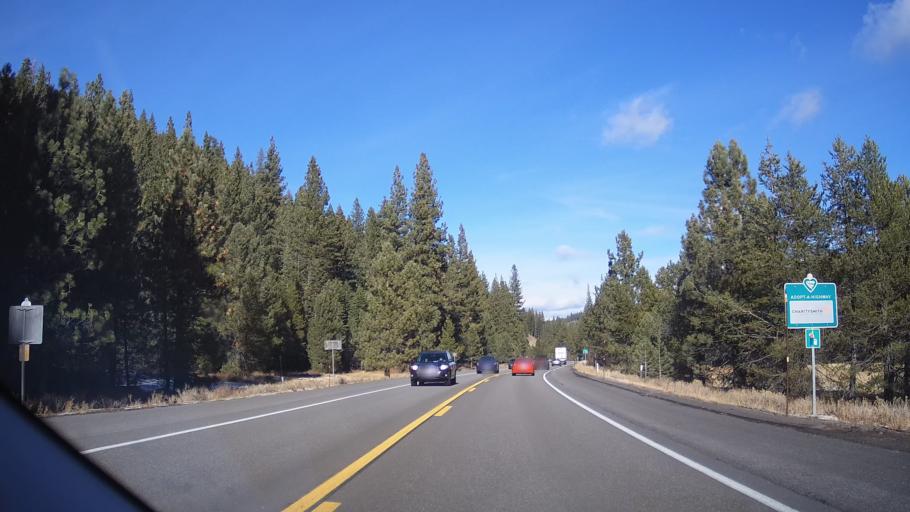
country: US
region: California
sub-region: Nevada County
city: Truckee
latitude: 39.2597
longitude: -120.2115
